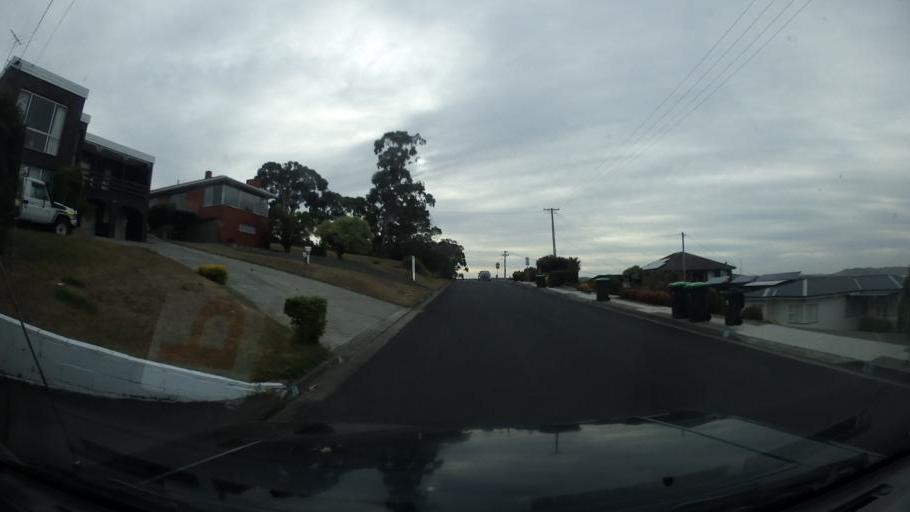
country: AU
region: Tasmania
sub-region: Clarence
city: Bellerive
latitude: -42.8714
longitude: 147.3781
